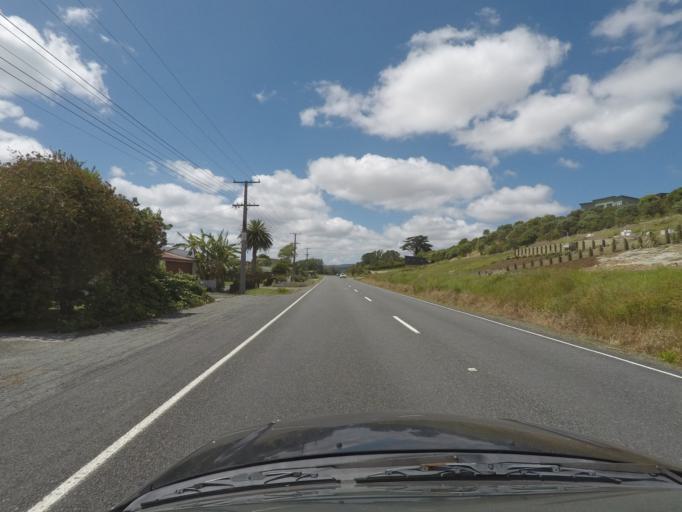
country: NZ
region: Northland
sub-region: Whangarei
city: Ruakaka
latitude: -35.9948
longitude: 174.4715
